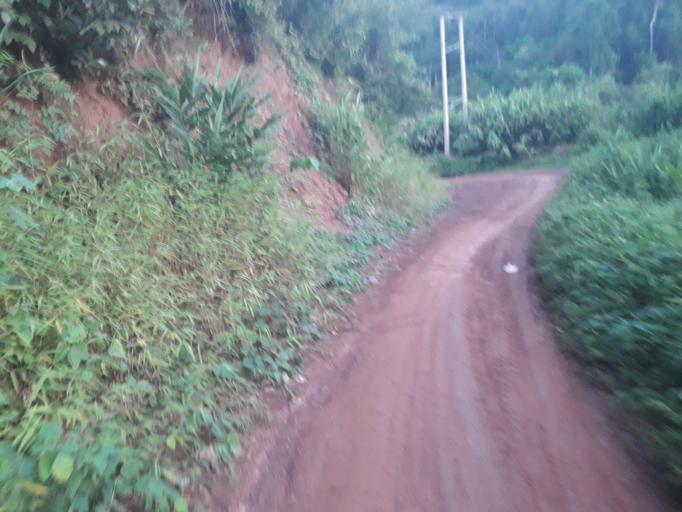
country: CN
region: Yunnan
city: Menglie
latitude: 22.1212
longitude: 101.7734
